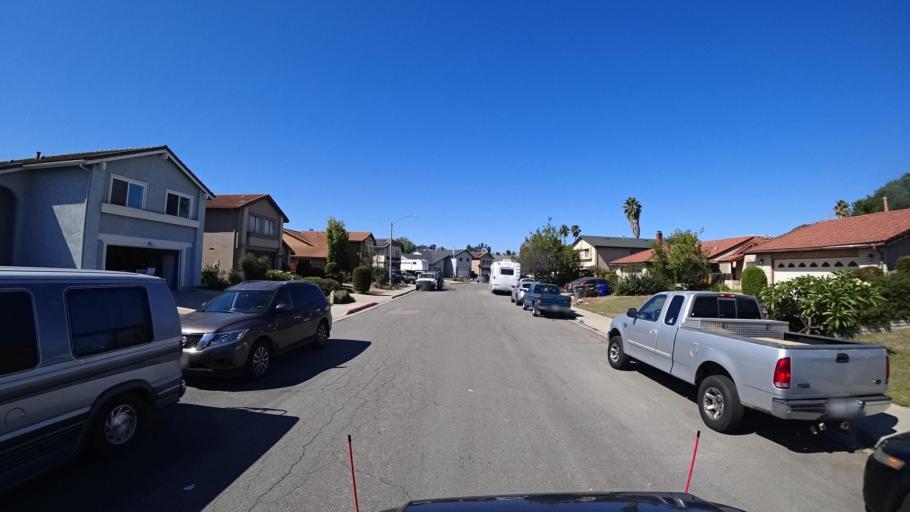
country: US
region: California
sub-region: San Diego County
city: La Presa
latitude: 32.6981
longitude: -117.0013
